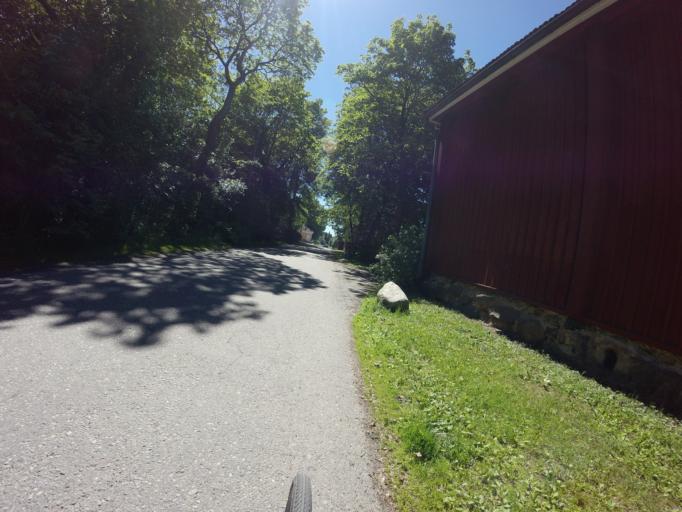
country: FI
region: Varsinais-Suomi
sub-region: Turku
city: Turku
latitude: 60.4744
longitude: 22.2933
